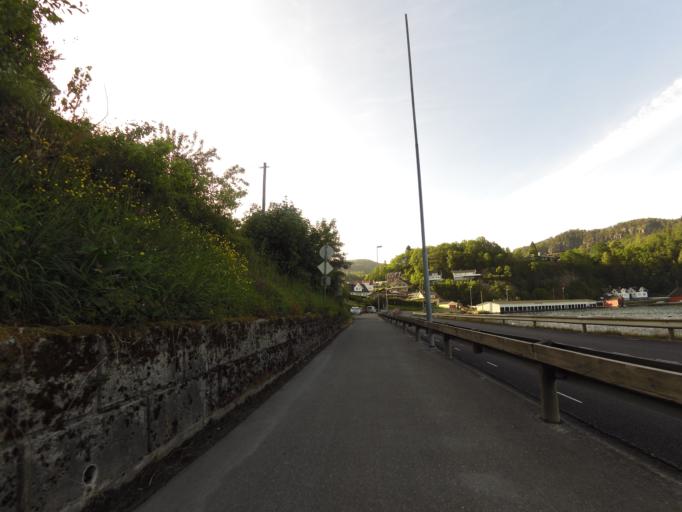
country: NO
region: Vest-Agder
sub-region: Flekkefjord
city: Flekkefjord
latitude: 58.2934
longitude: 6.6472
